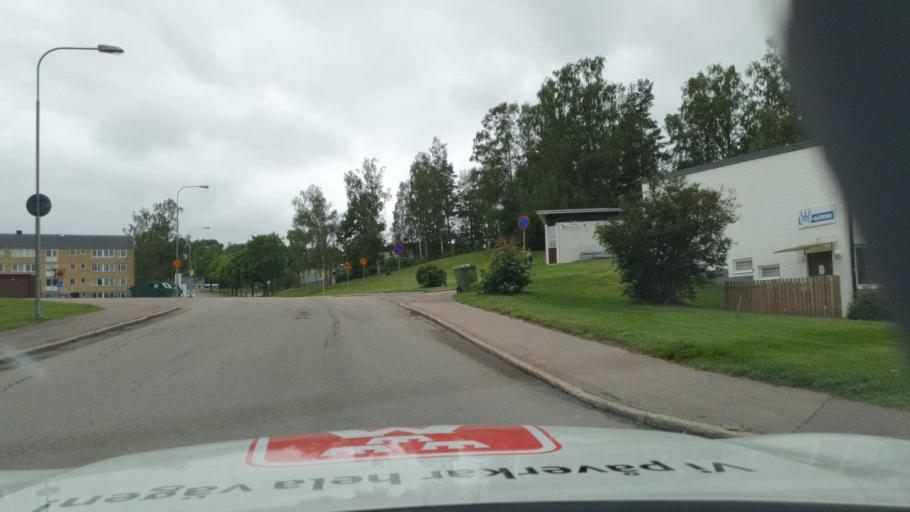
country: SE
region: Vaermland
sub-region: Grums Kommun
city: Grums
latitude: 59.3530
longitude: 13.1090
